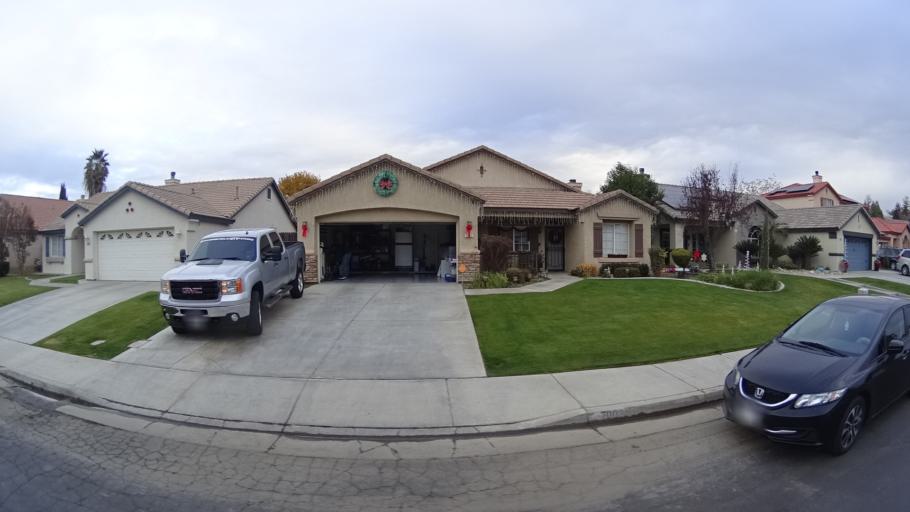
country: US
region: California
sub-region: Kern County
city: Greenfield
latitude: 35.2998
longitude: -119.0799
